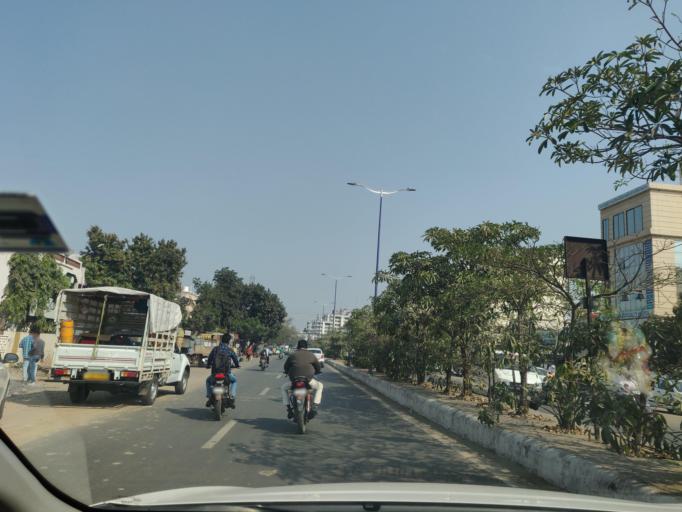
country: IN
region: Gujarat
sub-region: Vadodara
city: Vadodara
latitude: 22.2979
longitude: 73.2299
